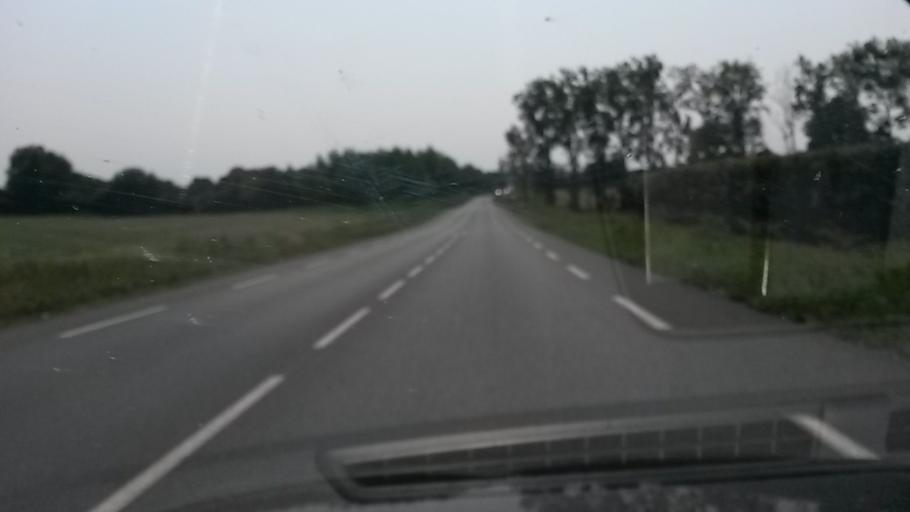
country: FR
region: Pays de la Loire
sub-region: Departement de la Mayenne
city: Chemaze
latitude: 47.7601
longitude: -0.7876
